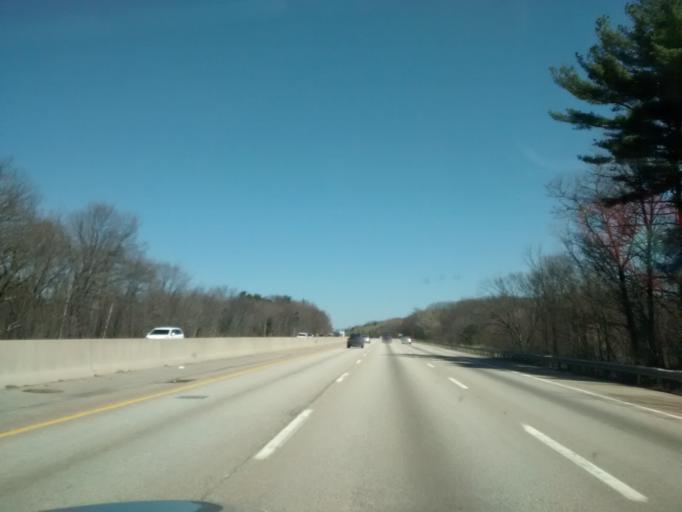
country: US
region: Massachusetts
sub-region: Worcester County
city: Grafton
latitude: 42.2230
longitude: -71.7207
